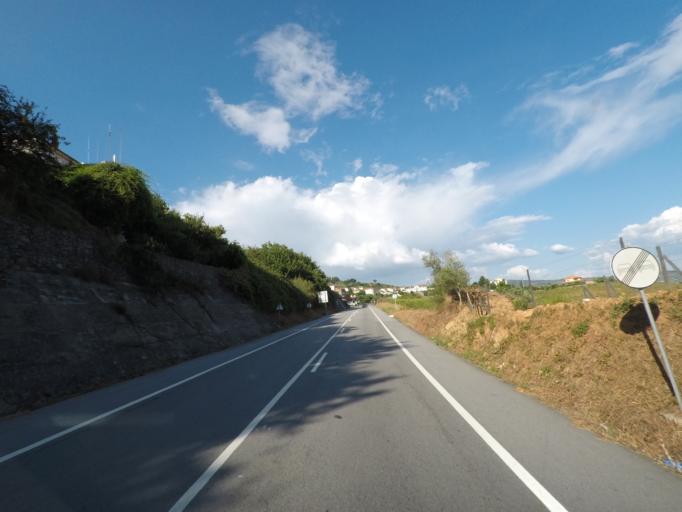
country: PT
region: Vila Real
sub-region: Mesao Frio
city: Mesao Frio
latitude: 41.1571
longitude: -7.8921
